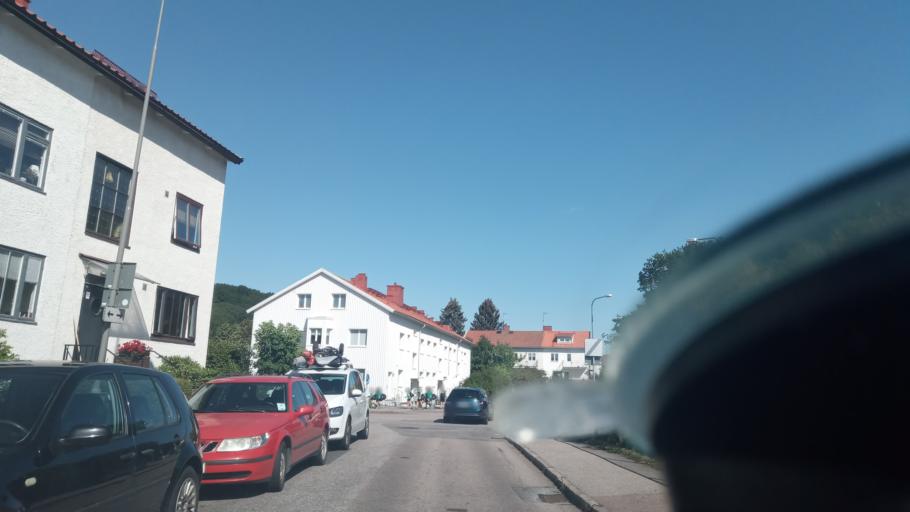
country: SE
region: Vaestra Goetaland
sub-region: Molndal
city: Moelndal
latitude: 57.6901
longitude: 12.0064
